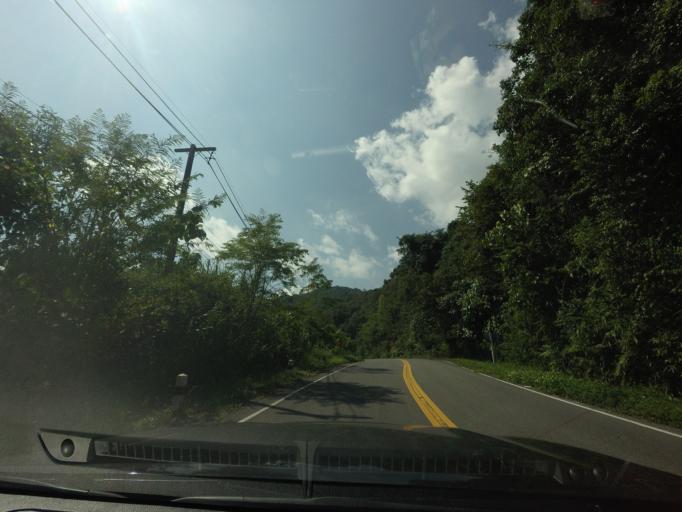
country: TH
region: Nan
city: Bo Kluea
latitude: 19.0587
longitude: 101.0928
